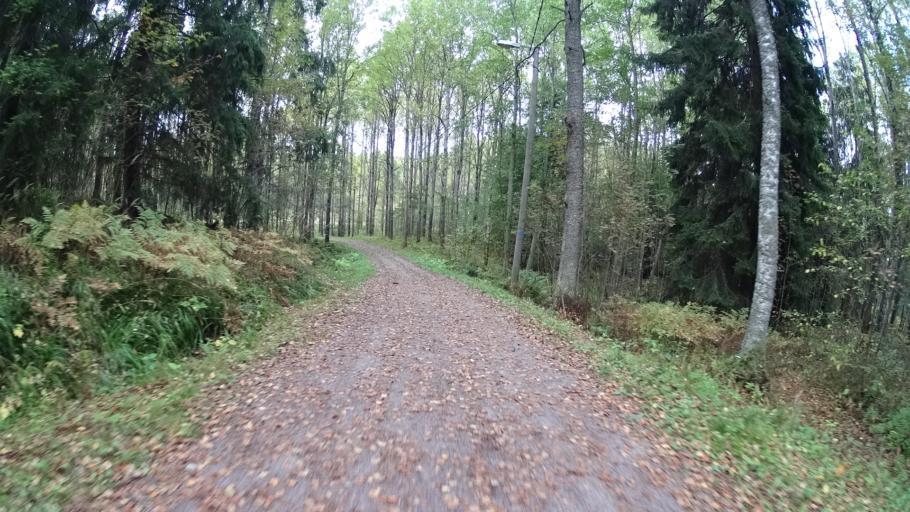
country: FI
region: Uusimaa
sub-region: Helsinki
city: Kauniainen
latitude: 60.1989
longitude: 24.6980
